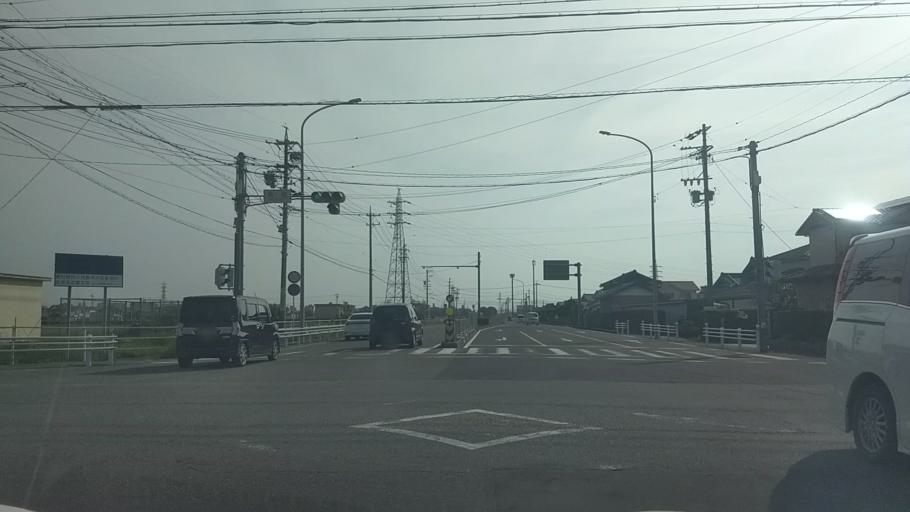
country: JP
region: Aichi
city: Anjo
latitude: 34.9695
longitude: 137.0756
